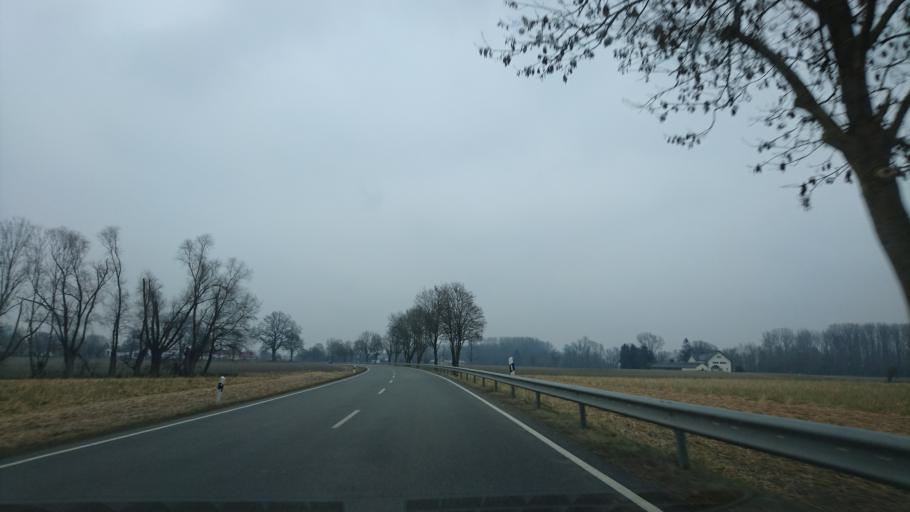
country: DE
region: Bavaria
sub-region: Lower Bavaria
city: Pocking
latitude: 48.4250
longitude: 13.3147
